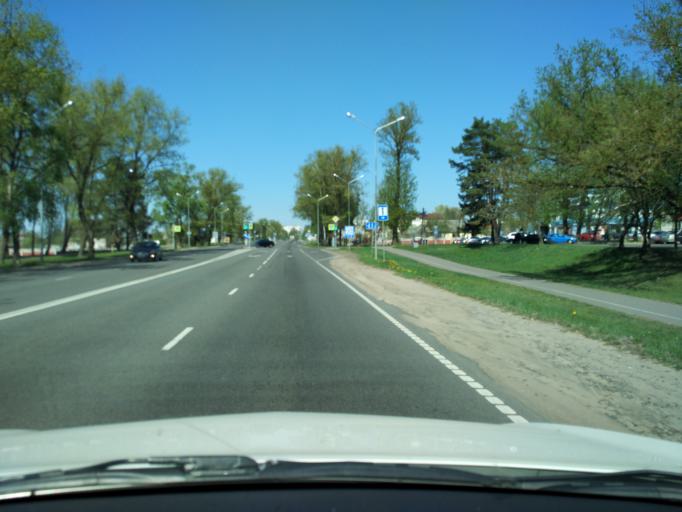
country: BY
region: Minsk
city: Borovlyany
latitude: 53.9938
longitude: 27.6718
